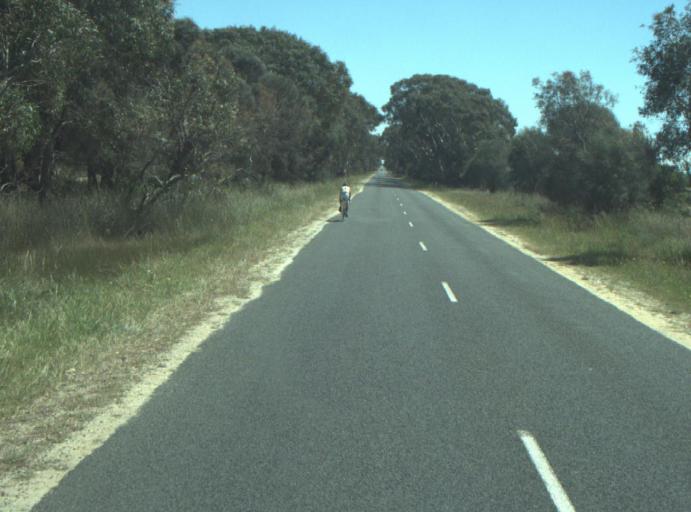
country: AU
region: Victoria
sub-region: Greater Geelong
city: Breakwater
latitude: -38.2444
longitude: 144.3520
